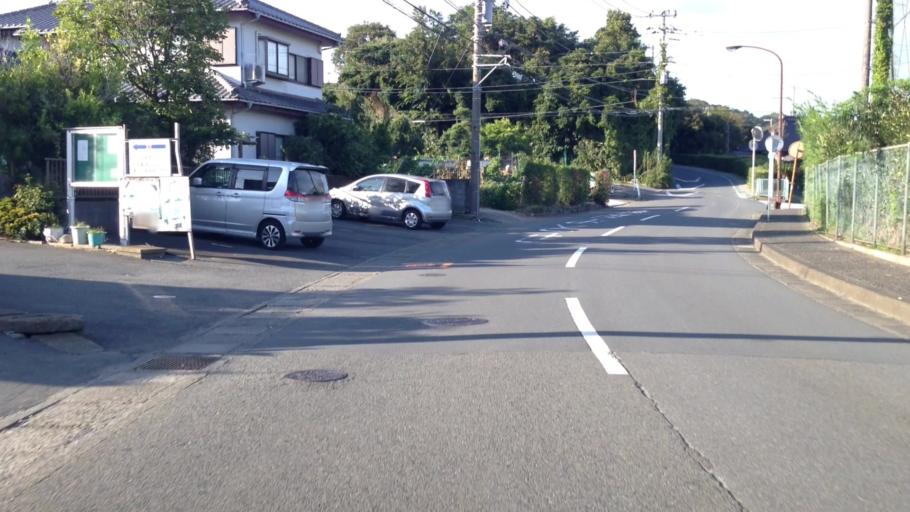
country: JP
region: Kanagawa
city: Yokosuka
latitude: 35.2285
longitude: 139.6289
